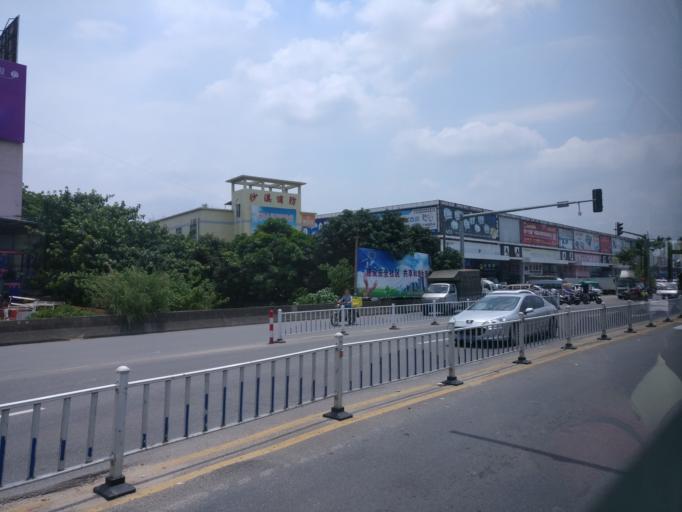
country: CN
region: Guangdong
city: Dashi
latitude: 23.0376
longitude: 113.3263
